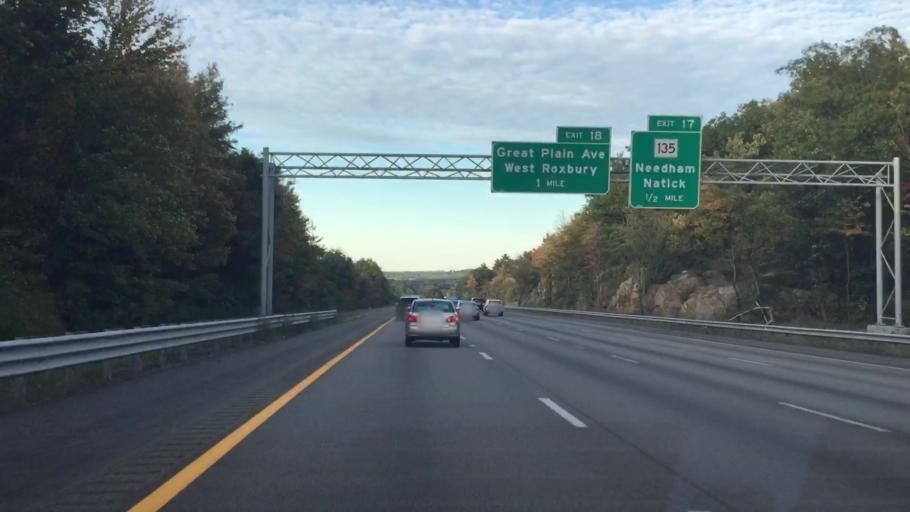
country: US
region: Massachusetts
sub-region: Norfolk County
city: Needham
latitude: 42.2574
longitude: -71.2083
